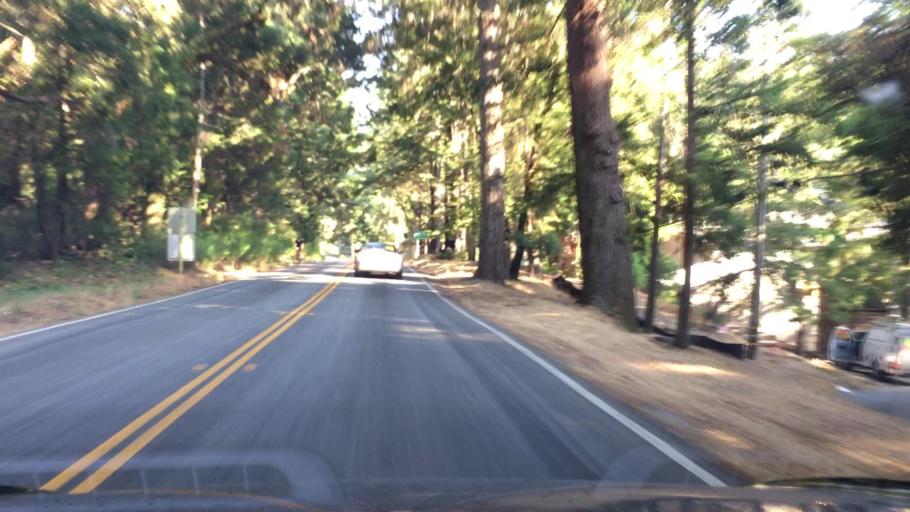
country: US
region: California
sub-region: San Mateo County
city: Portola Valley
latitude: 37.3881
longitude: -122.2671
